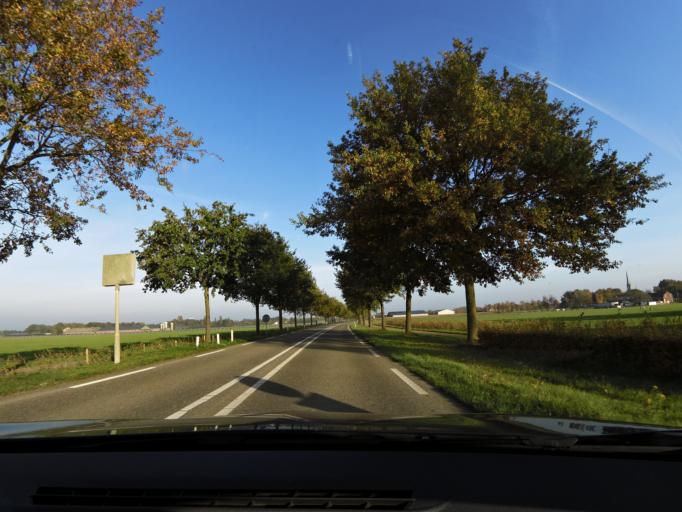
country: NL
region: North Brabant
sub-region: Gemeente Made en Drimmelen
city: Made
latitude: 51.6692
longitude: 4.7370
